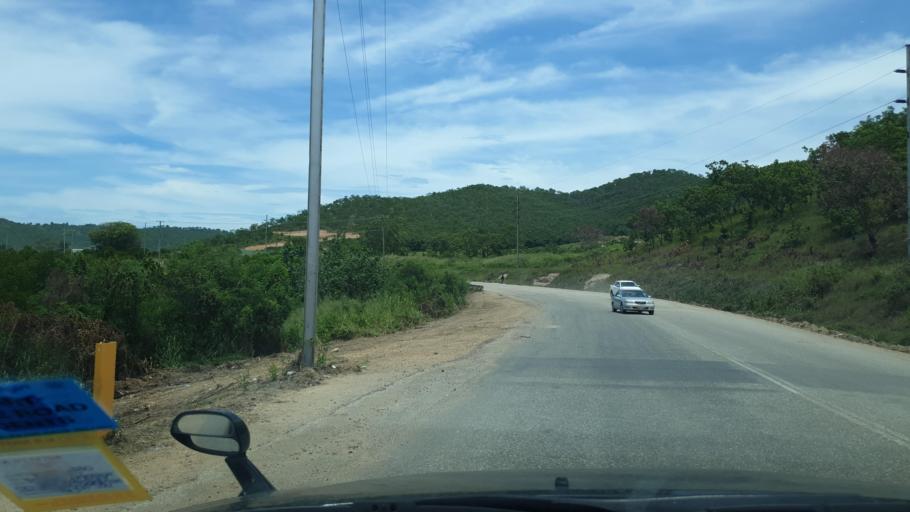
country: PG
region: National Capital
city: Port Moresby
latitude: -9.4195
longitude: 147.0963
